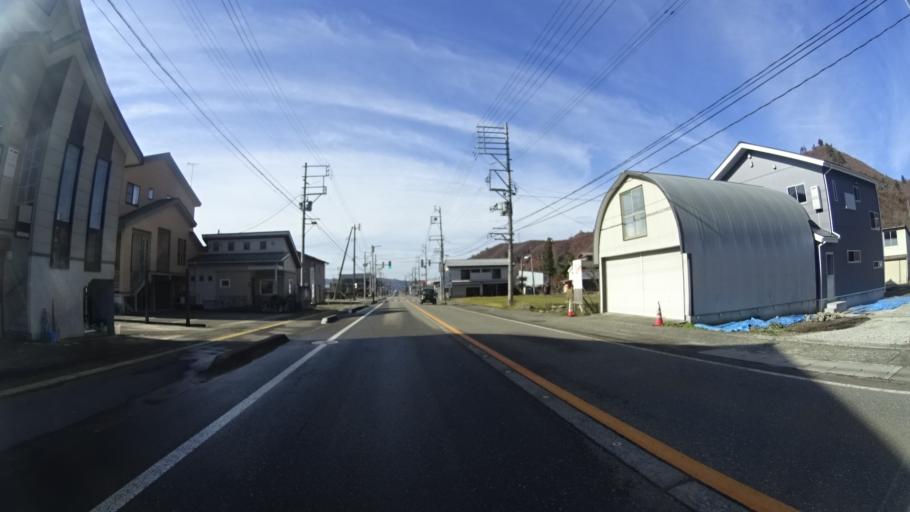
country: JP
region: Niigata
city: Muikamachi
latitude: 37.2266
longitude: 139.0042
